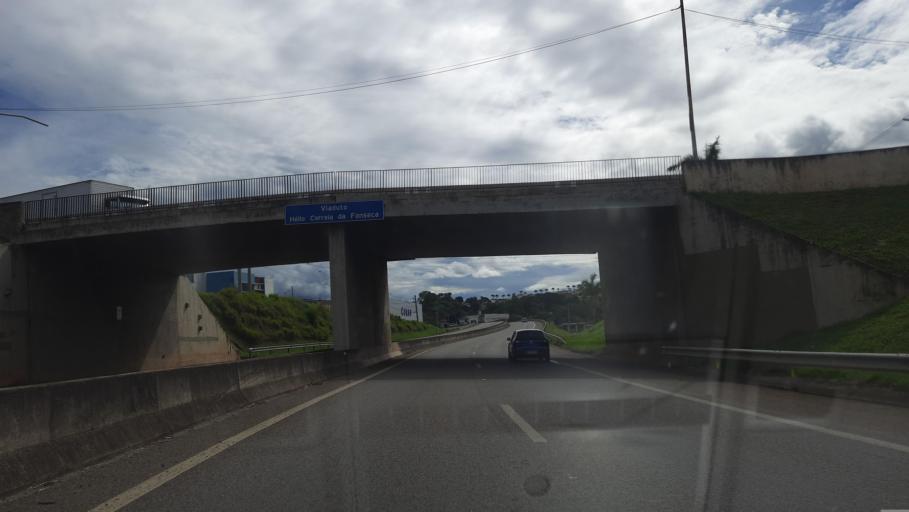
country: BR
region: Sao Paulo
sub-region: Sao Joao Da Boa Vista
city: Sao Joao da Boa Vista
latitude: -21.9789
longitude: -46.7829
